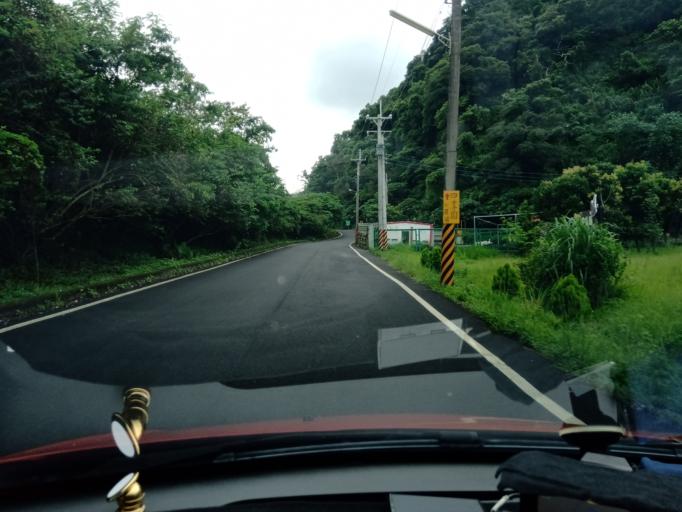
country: TW
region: Taiwan
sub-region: Yilan
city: Yilan
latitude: 24.7817
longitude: 121.7069
